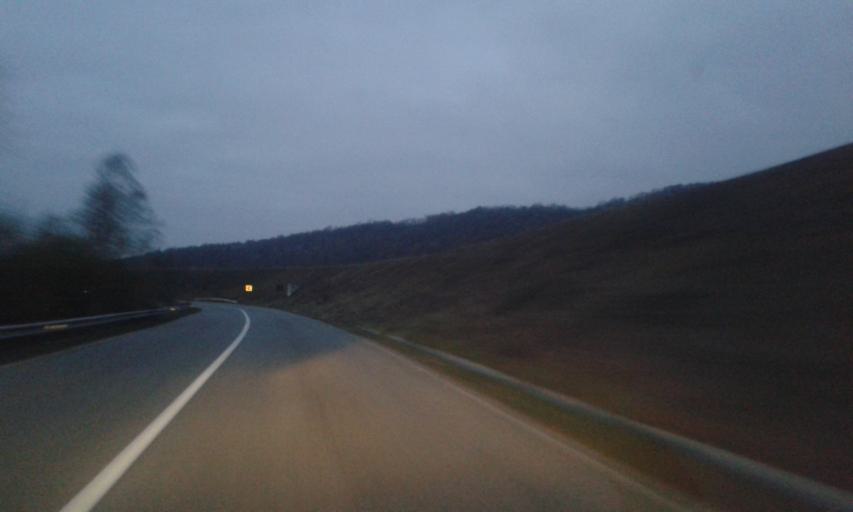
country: RO
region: Gorj
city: Targu Jiu
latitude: 45.0669
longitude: 23.2786
